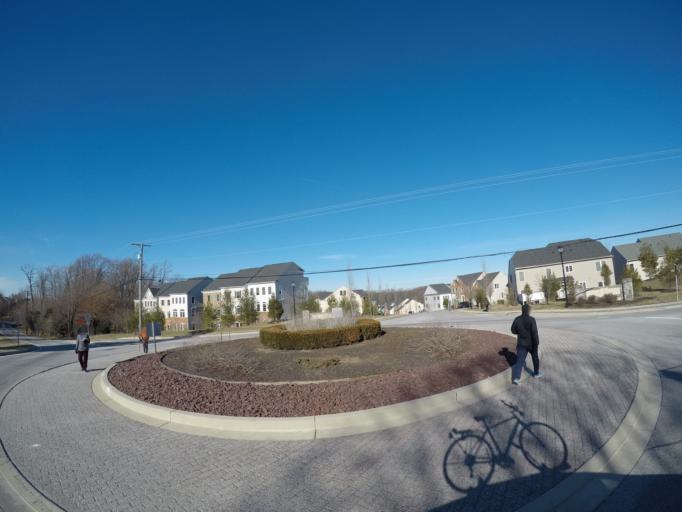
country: US
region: Maryland
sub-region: Howard County
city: Ellicott City
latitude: 39.2572
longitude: -76.7913
